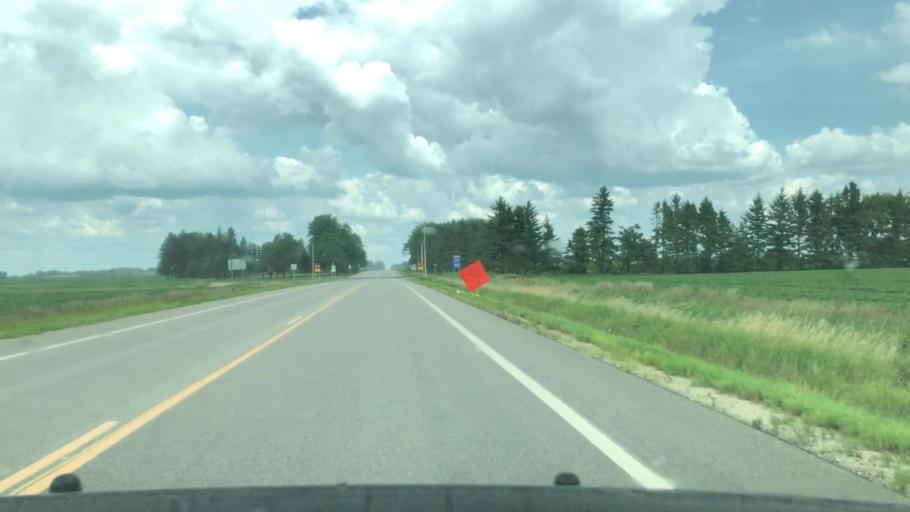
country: US
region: Minnesota
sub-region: Olmsted County
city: Stewartville
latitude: 43.8904
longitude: -92.5285
